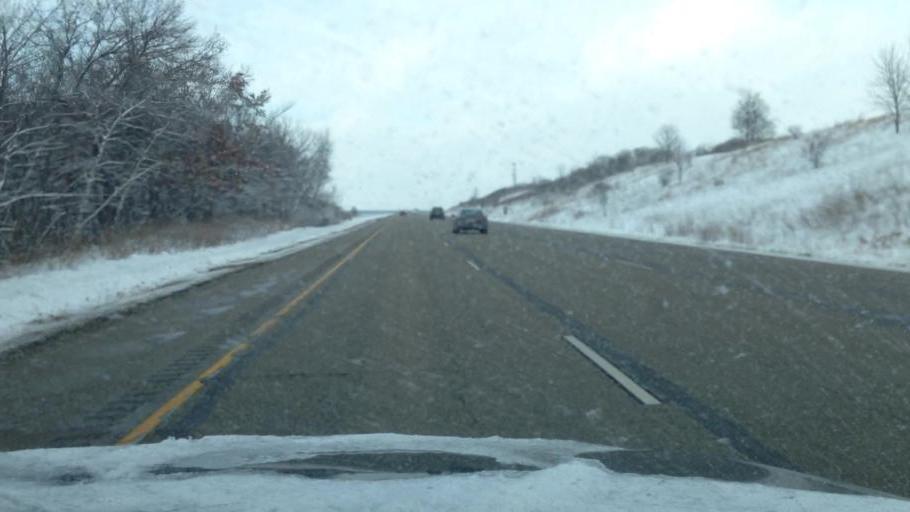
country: US
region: Wisconsin
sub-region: Walworth County
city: East Troy
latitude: 42.7345
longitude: -88.4565
